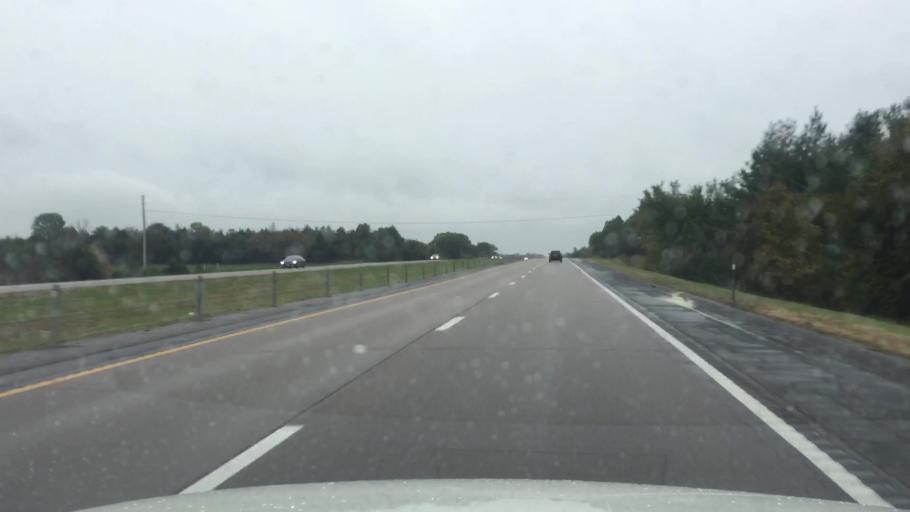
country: US
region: Missouri
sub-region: Boone County
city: Ashland
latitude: 38.7211
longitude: -92.2545
